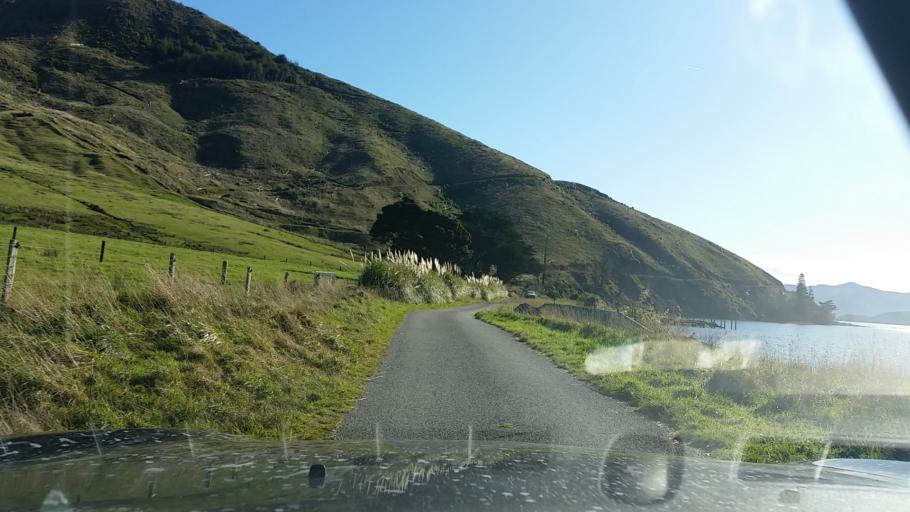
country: NZ
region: Marlborough
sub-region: Marlborough District
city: Picton
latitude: -41.1118
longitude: 174.0341
